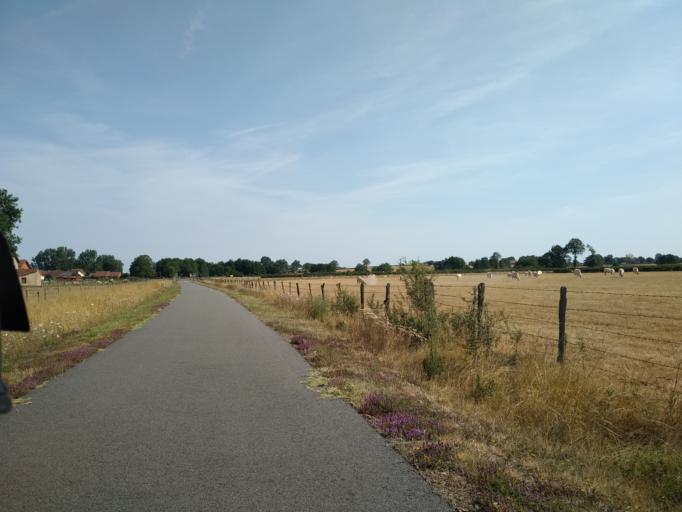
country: FR
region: Bourgogne
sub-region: Departement de Saone-et-Loire
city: Marcigny
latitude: 46.2994
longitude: 4.0301
